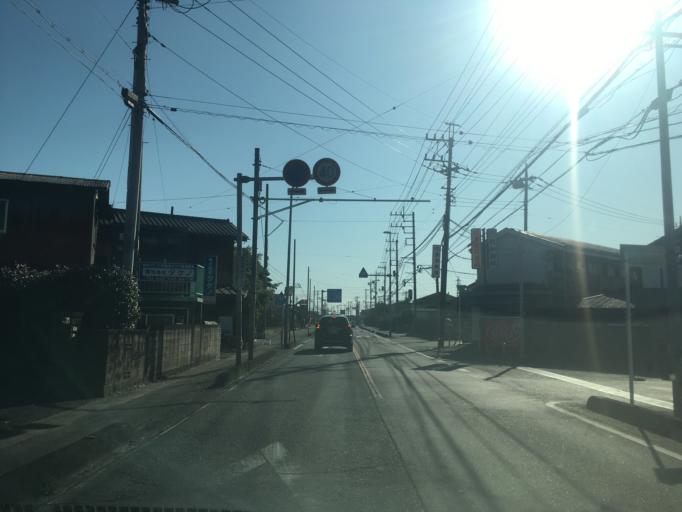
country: JP
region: Saitama
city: Tokorozawa
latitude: 35.8373
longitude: 139.4659
